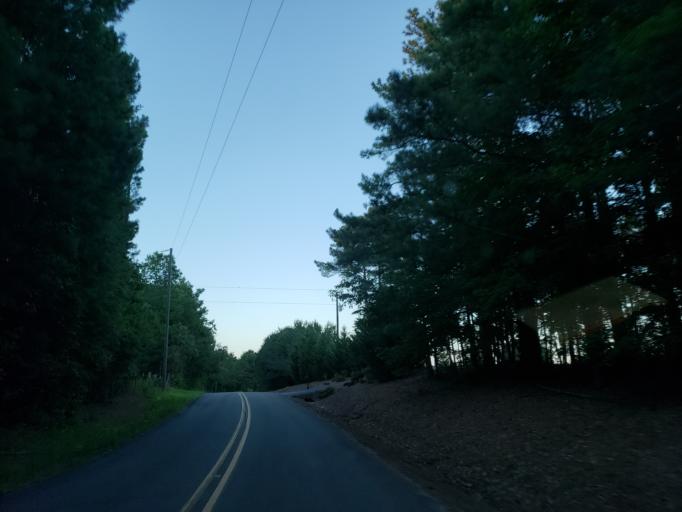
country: US
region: Georgia
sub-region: Bartow County
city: Emerson
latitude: 34.0585
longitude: -84.8338
